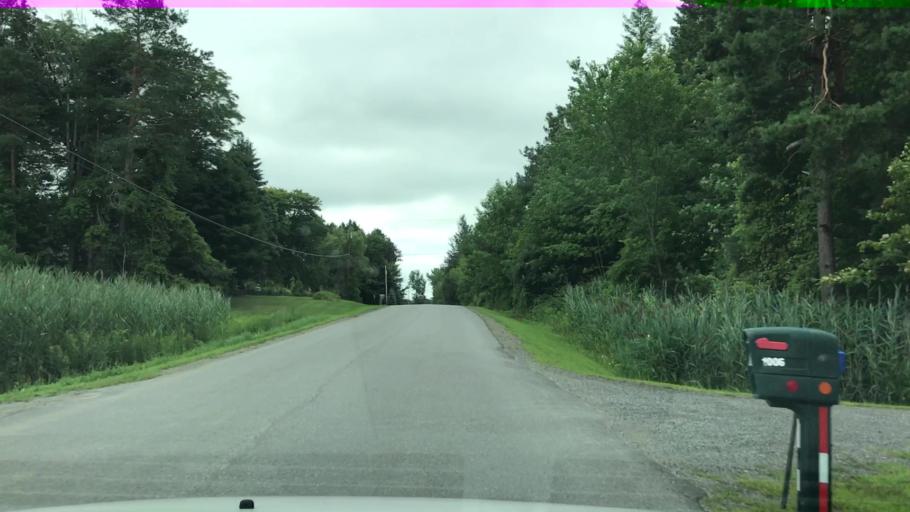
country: US
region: New York
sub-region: Wyoming County
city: Attica
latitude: 42.8334
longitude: -78.3365
